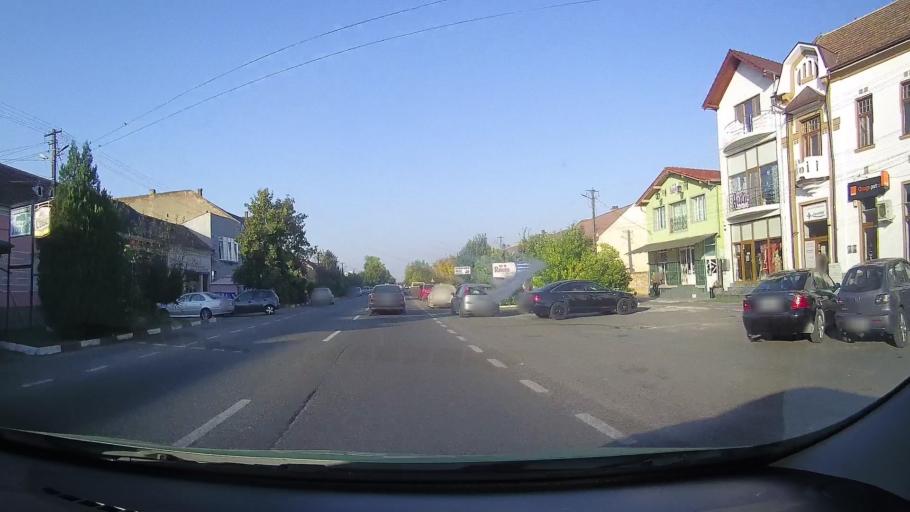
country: RO
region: Arad
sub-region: Comuna Pancota
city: Pancota
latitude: 46.3254
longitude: 21.6889
